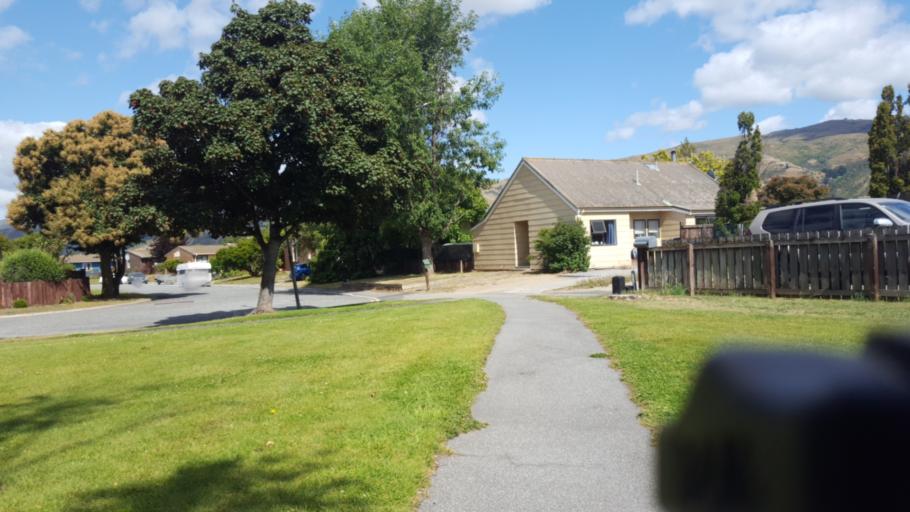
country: NZ
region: Otago
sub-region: Queenstown-Lakes District
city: Wanaka
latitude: -45.0403
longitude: 169.1838
